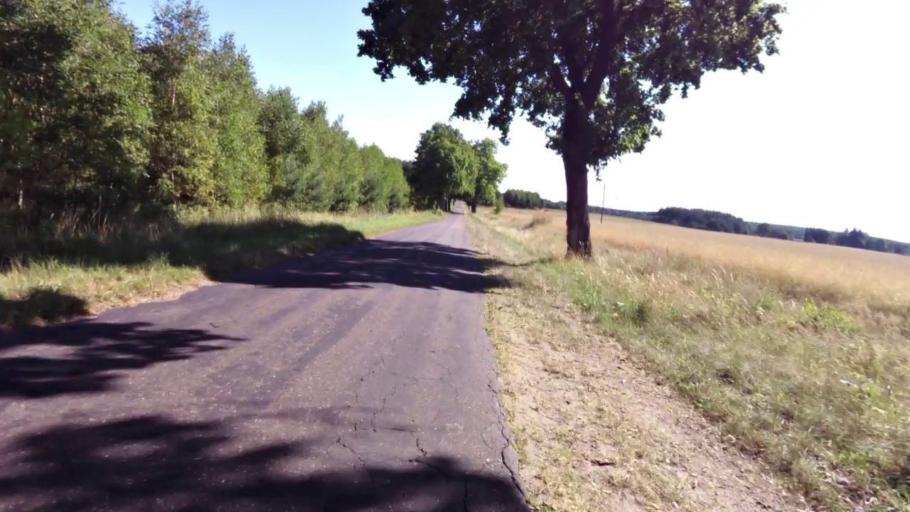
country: PL
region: West Pomeranian Voivodeship
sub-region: Powiat szczecinecki
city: Szczecinek
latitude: 53.7906
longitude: 16.6777
